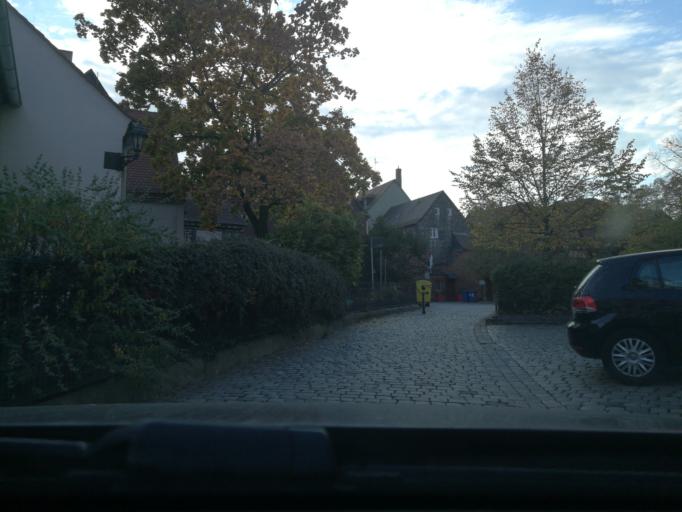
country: DE
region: Bavaria
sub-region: Regierungsbezirk Mittelfranken
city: Furth
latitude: 49.4797
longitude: 10.9889
